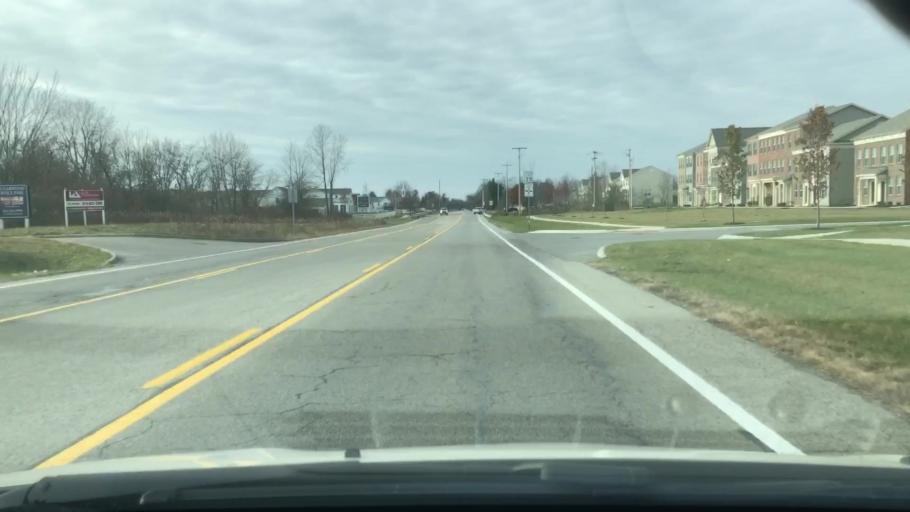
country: US
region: Ohio
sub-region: Franklin County
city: New Albany
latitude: 40.0988
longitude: -82.8282
